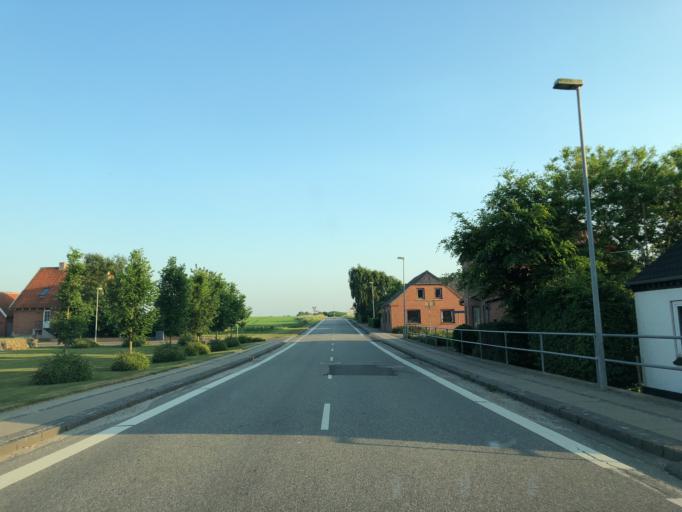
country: DK
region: Central Jutland
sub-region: Struer Kommune
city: Struer
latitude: 56.4713
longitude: 8.5480
